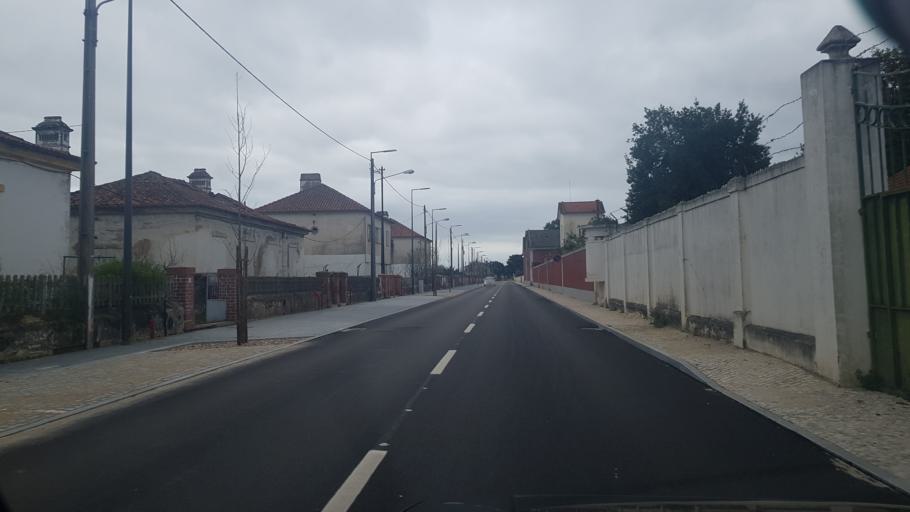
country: PT
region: Santarem
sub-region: Entroncamento
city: Entroncamento
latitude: 39.4619
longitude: -8.4792
